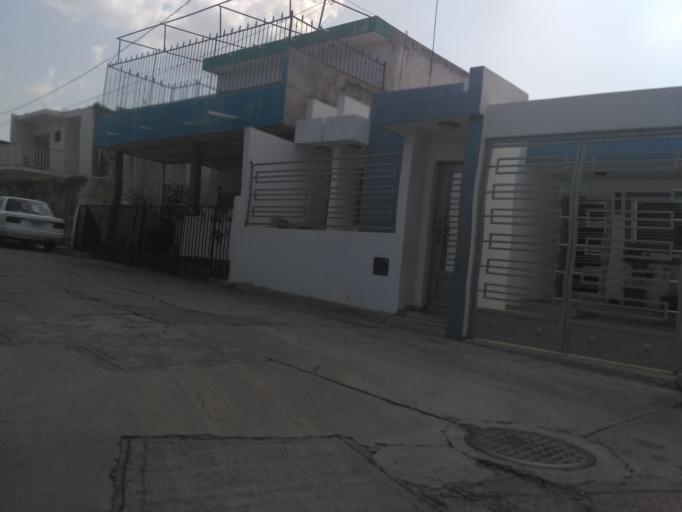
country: MX
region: Sinaloa
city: Culiacan
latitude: 24.7942
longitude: -107.4031
